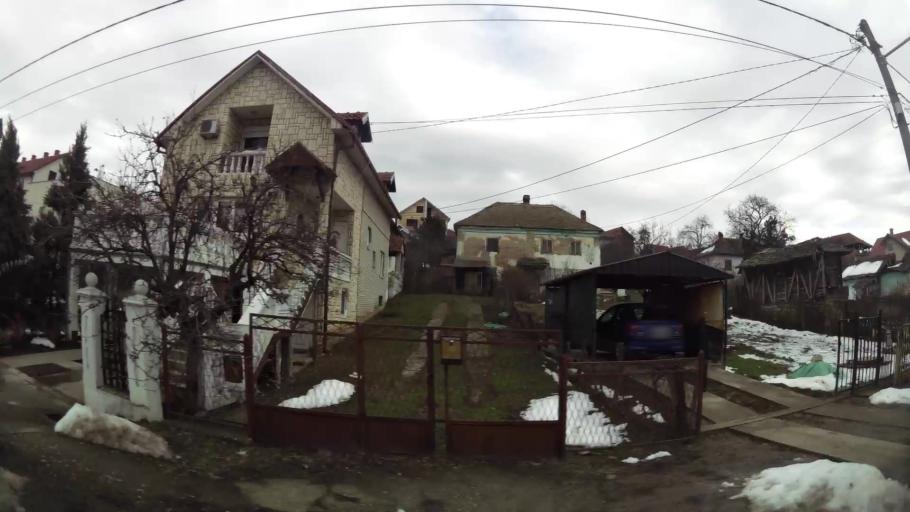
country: RS
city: Ostruznica
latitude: 44.7256
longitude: 20.3712
